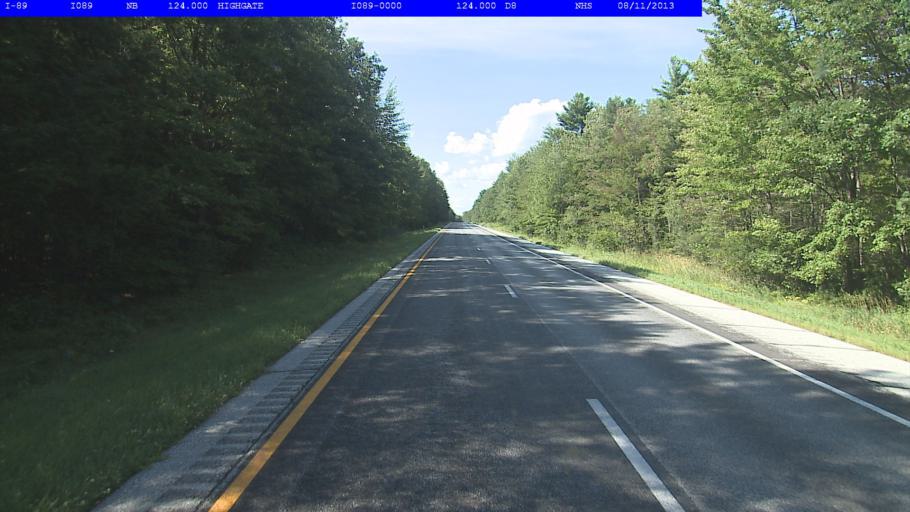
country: US
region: Vermont
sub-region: Franklin County
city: Swanton
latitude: 44.9310
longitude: -73.1113
